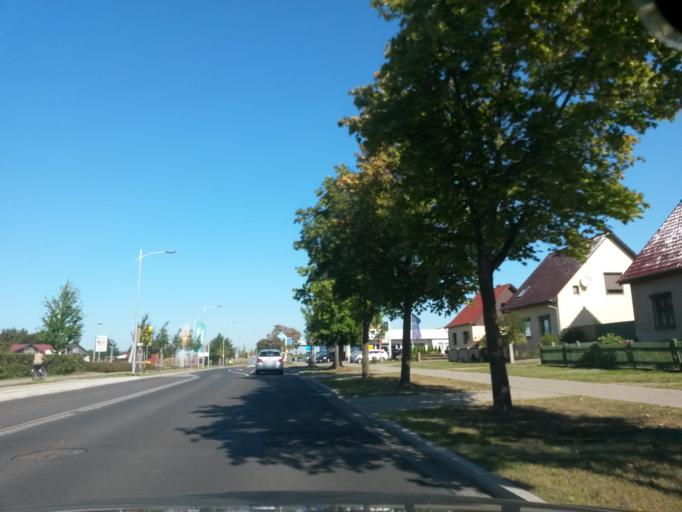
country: DE
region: Brandenburg
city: Templin
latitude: 53.1276
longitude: 13.4907
